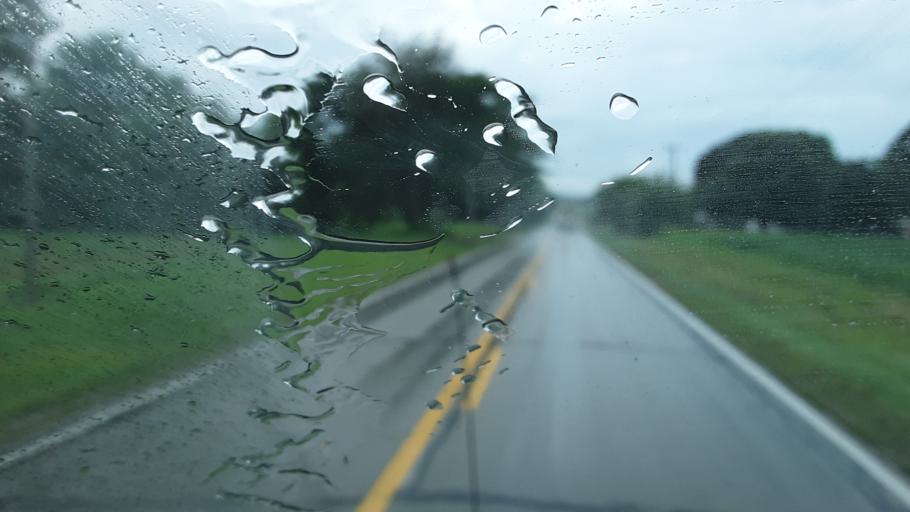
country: US
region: Kentucky
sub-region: Logan County
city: Russellville
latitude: 36.8124
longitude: -86.9426
